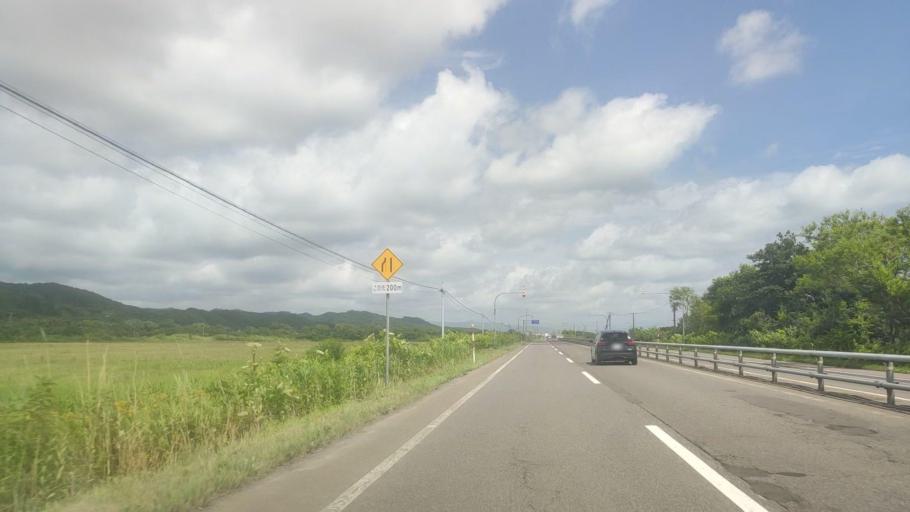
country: JP
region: Hokkaido
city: Niseko Town
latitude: 42.4178
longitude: 140.3110
